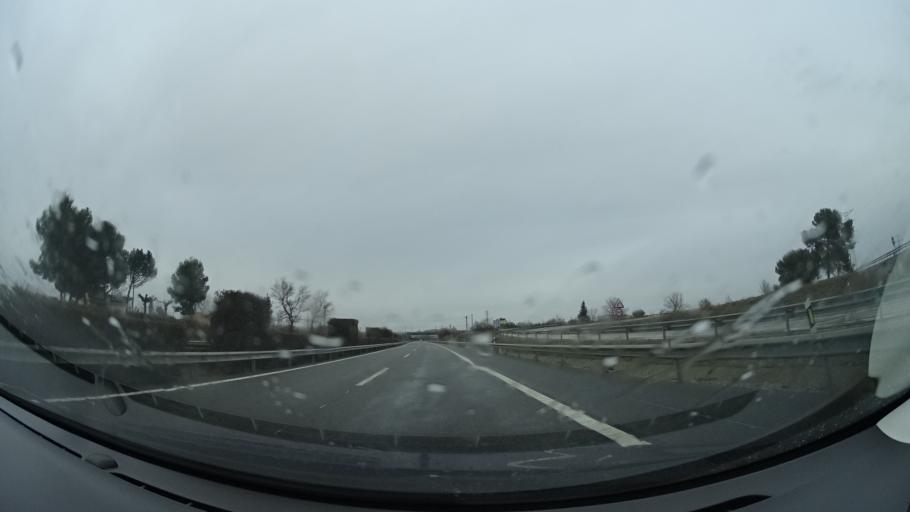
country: ES
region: Catalonia
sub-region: Provincia de Lleida
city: Lleida
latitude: 41.5820
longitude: 0.6241
